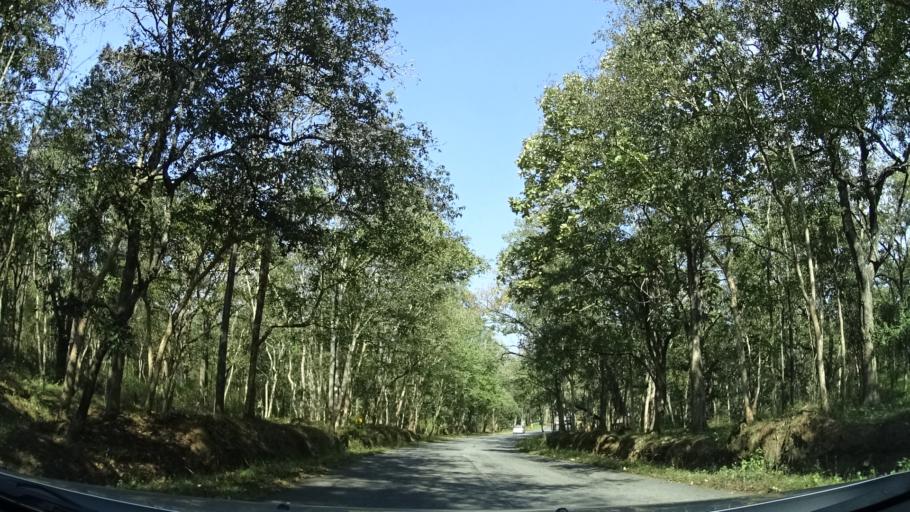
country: IN
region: Tamil Nadu
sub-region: Nilgiri
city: Naduvattam
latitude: 11.7108
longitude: 76.4168
